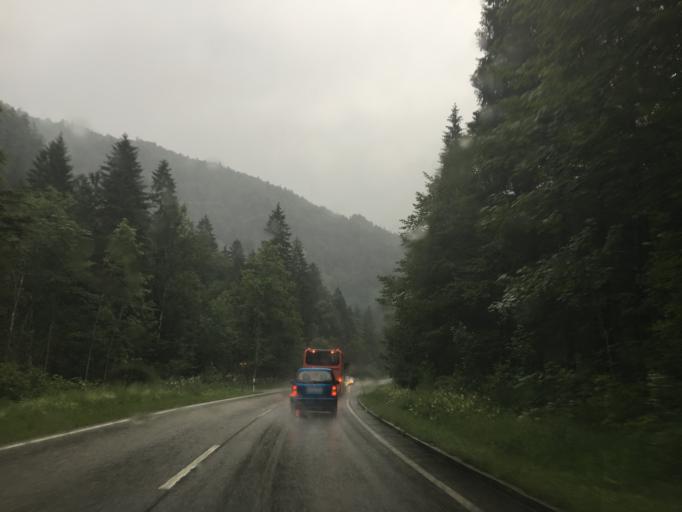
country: DE
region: Bavaria
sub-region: Upper Bavaria
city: Reit im Winkl
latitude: 47.6882
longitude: 12.5032
